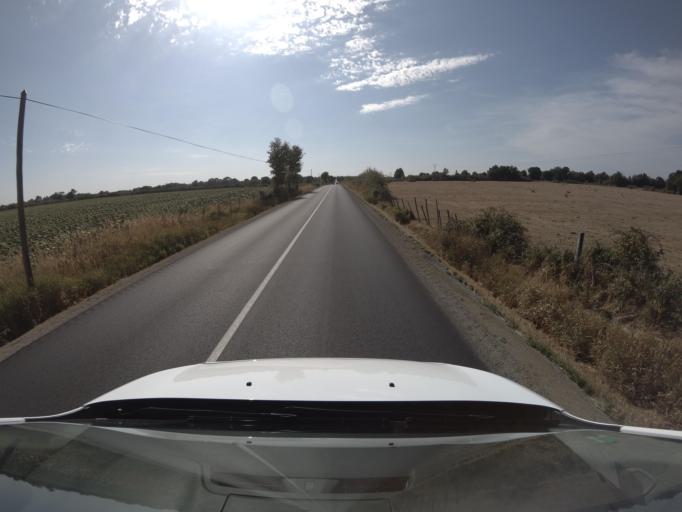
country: FR
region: Poitou-Charentes
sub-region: Departement des Deux-Sevres
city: Mauze-Thouarsais
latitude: 46.9990
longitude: -0.3031
